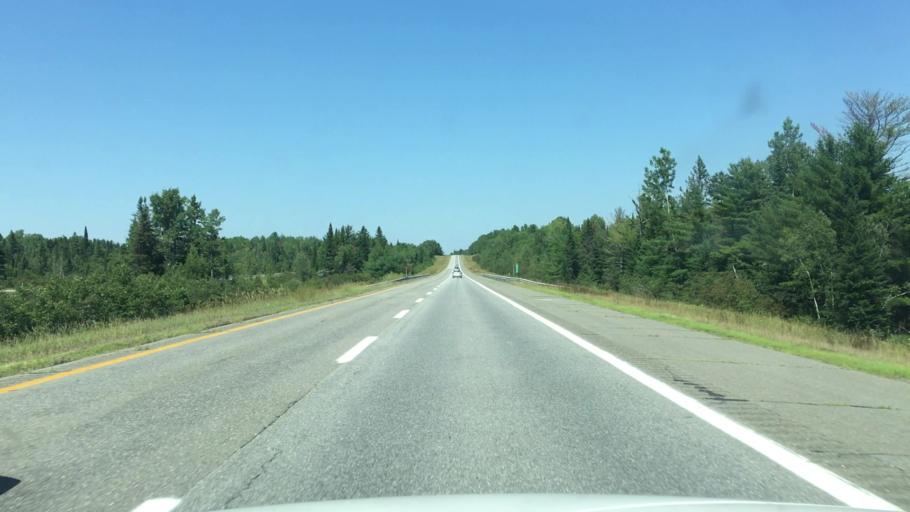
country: US
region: Maine
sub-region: Penobscot County
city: Howland
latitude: 45.1990
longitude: -68.6863
